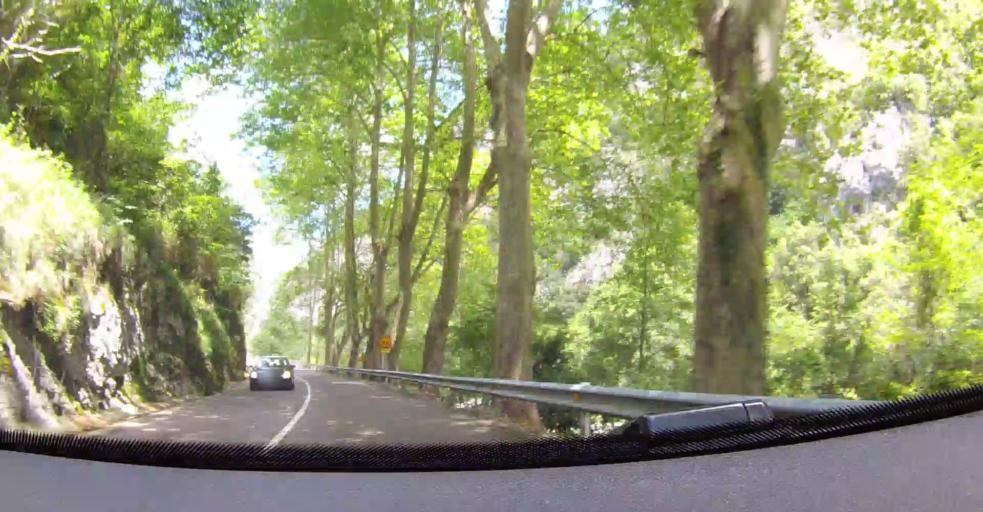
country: ES
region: Cantabria
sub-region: Provincia de Cantabria
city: Tresviso
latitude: 43.2964
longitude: -4.6072
